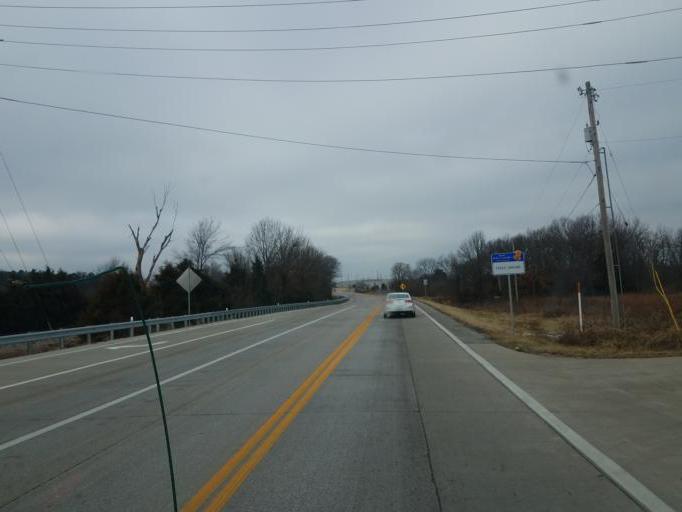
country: US
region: Missouri
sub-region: Greene County
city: Strafford
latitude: 37.2475
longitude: -93.1843
